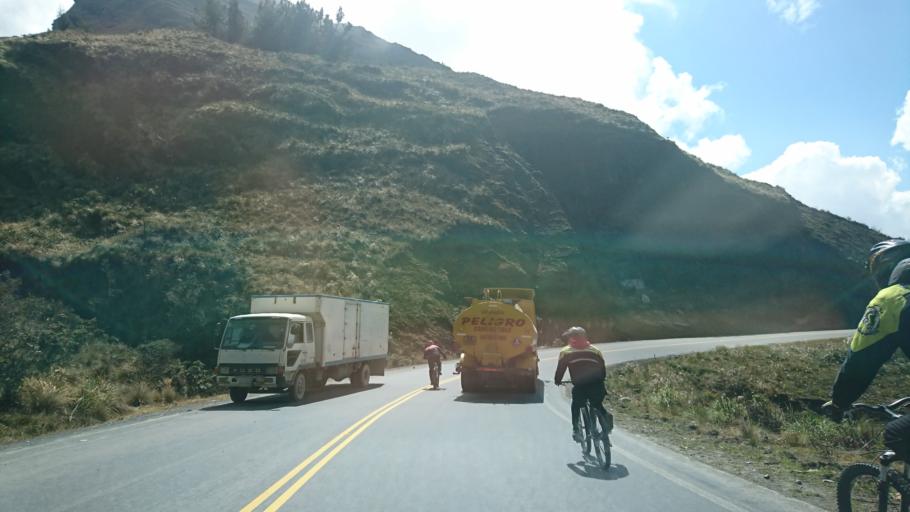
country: BO
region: La Paz
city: Coroico
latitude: -16.3248
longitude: -67.9408
